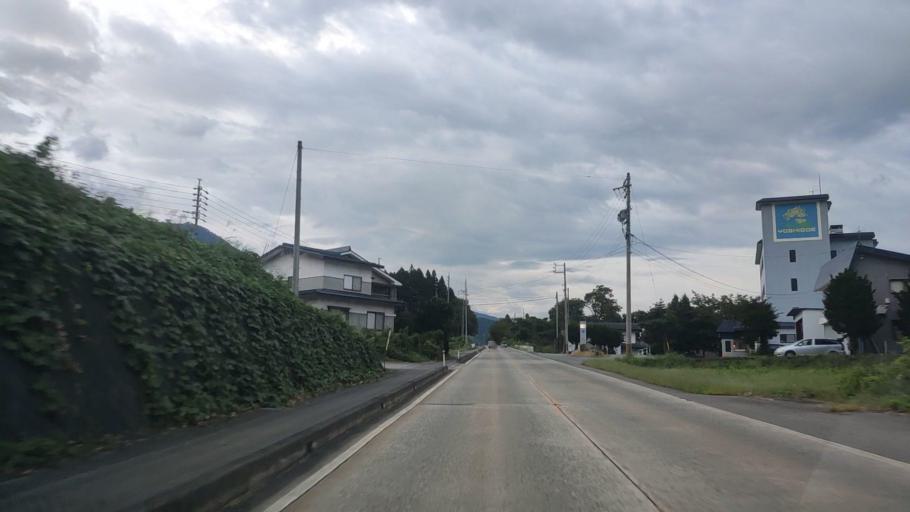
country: JP
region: Nagano
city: Iiyama
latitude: 36.8908
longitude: 138.4075
